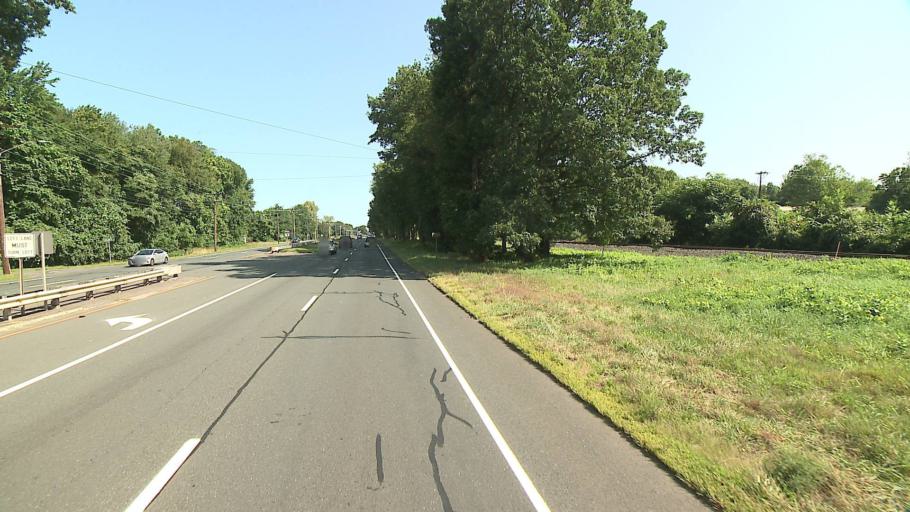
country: US
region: Connecticut
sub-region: Hartford County
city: South Windsor
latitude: 41.8274
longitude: -72.6063
